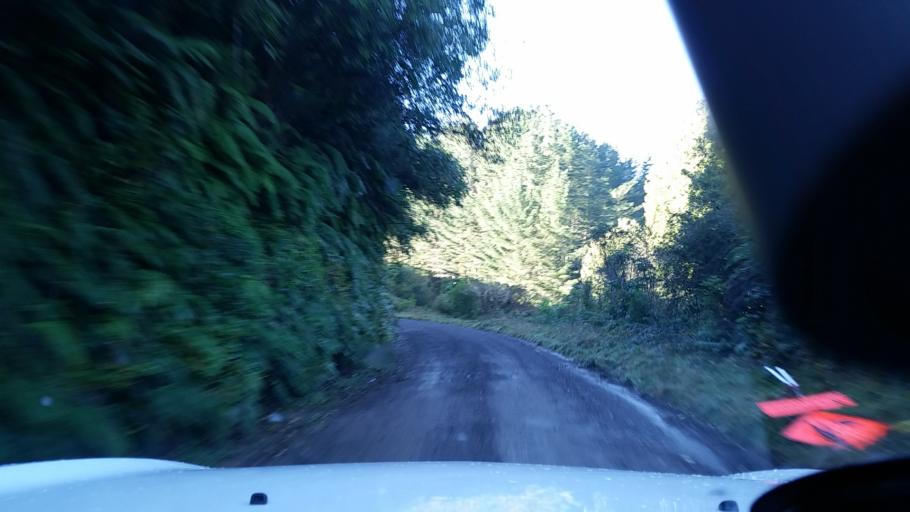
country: NZ
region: Bay of Plenty
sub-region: Kawerau District
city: Kawerau
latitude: -38.0025
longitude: 176.6037
